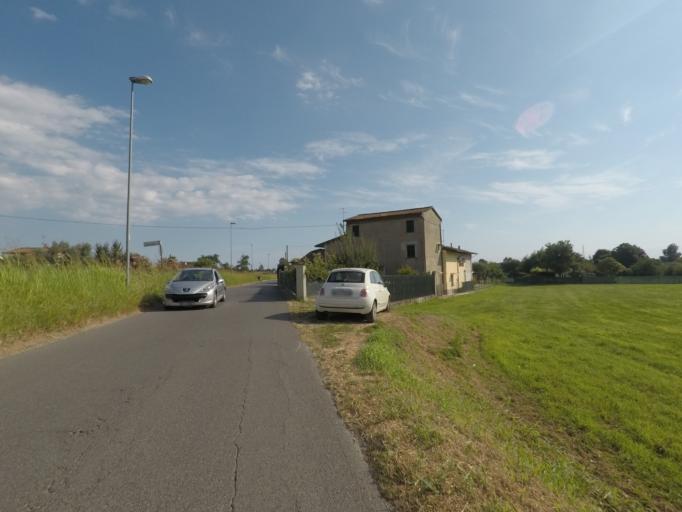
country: IT
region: Tuscany
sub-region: Provincia di Massa-Carrara
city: Capanne-Prato-Cinquale
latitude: 44.0116
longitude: 10.1490
